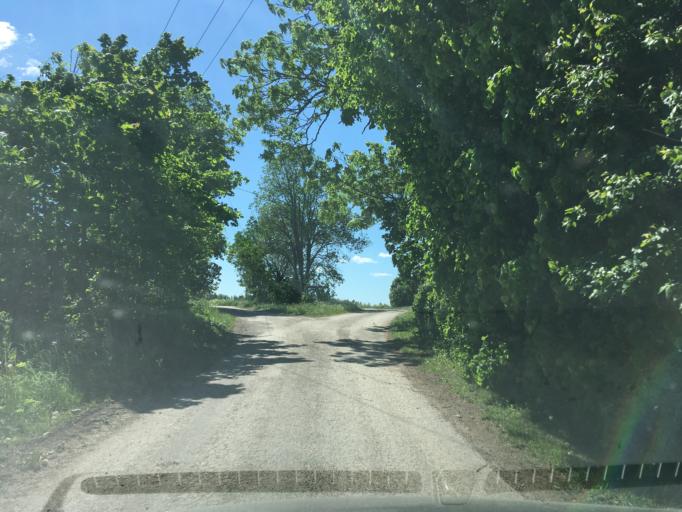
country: EE
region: Harju
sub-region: Rae vald
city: Vaida
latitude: 59.1581
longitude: 25.1263
